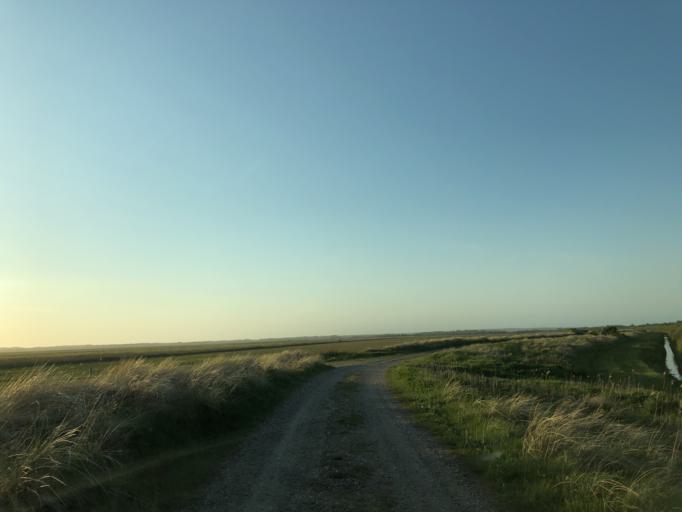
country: DK
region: Central Jutland
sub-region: Holstebro Kommune
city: Ulfborg
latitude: 56.2307
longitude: 8.1660
